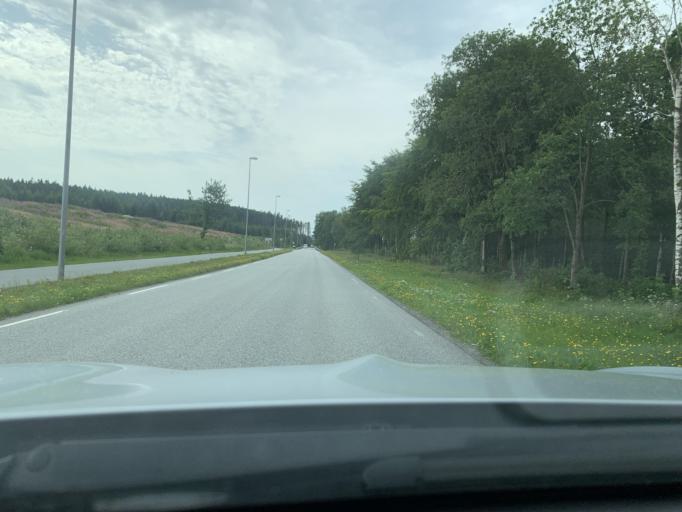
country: NO
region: Rogaland
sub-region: Time
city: Bryne
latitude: 58.7539
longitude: 5.6986
